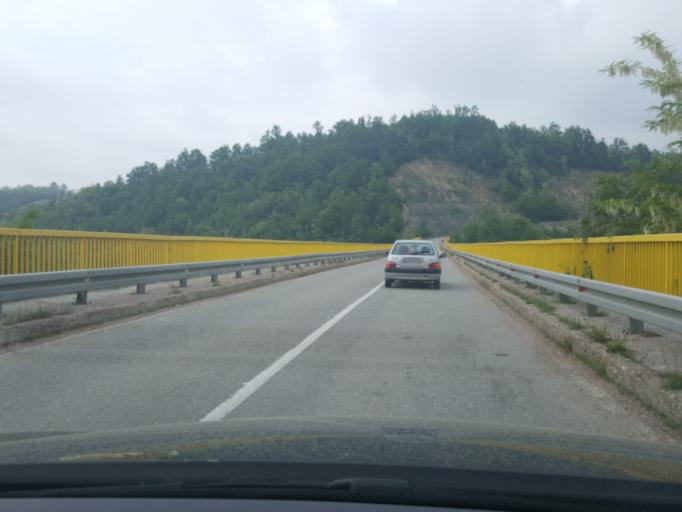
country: RS
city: Kamenica
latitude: 44.2399
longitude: 19.7207
